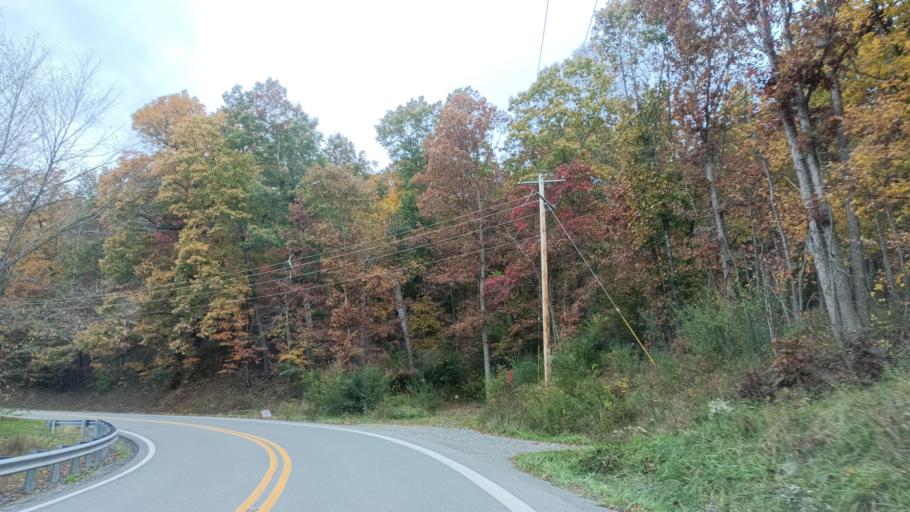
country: US
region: West Virginia
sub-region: Taylor County
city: Grafton
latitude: 39.3304
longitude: -79.9174
